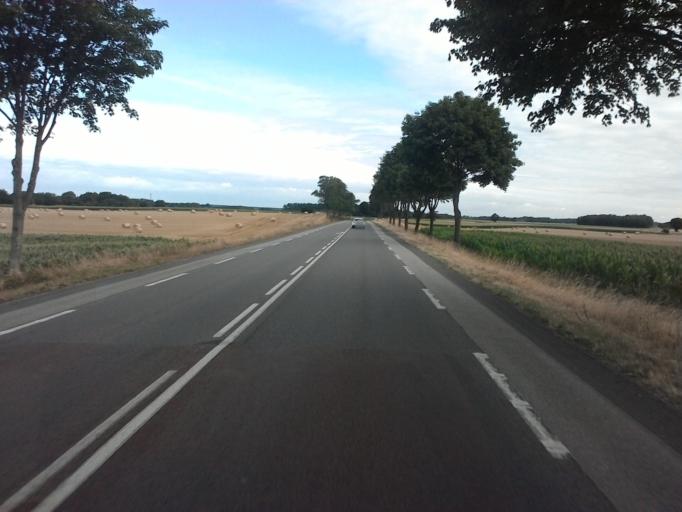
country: FR
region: Rhone-Alpes
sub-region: Departement de l'Ain
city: Tossiat
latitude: 46.1139
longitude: 5.3004
